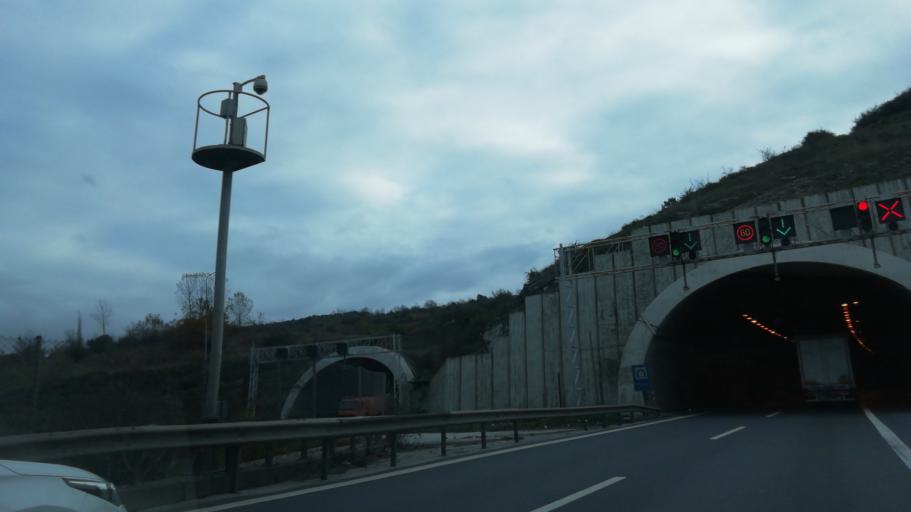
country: TR
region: Kocaeli
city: Izmit
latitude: 40.7787
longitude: 29.8878
